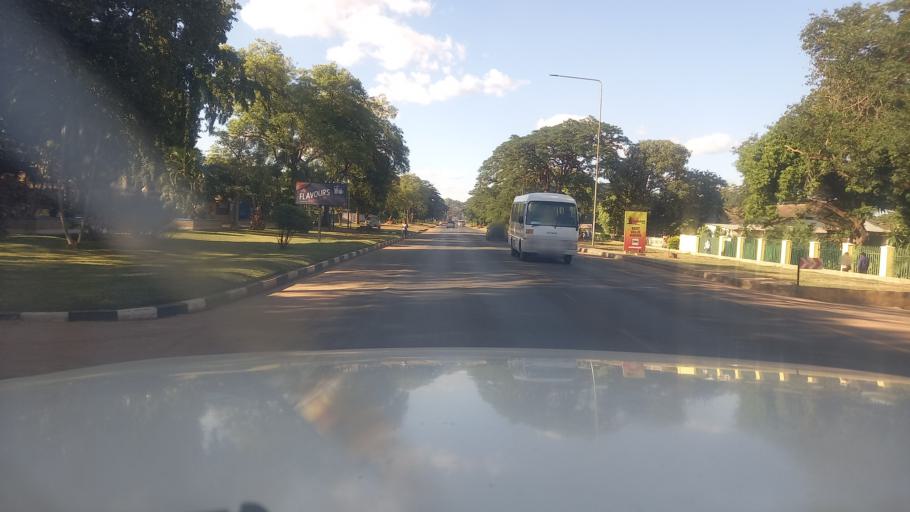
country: ZM
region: Southern
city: Livingstone
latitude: -17.8422
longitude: 25.8615
